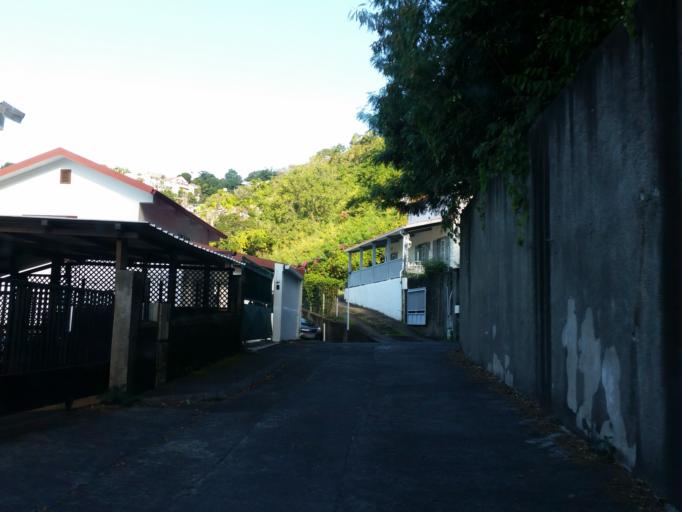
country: RE
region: Reunion
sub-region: Reunion
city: Saint-Denis
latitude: -20.9009
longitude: 55.4579
